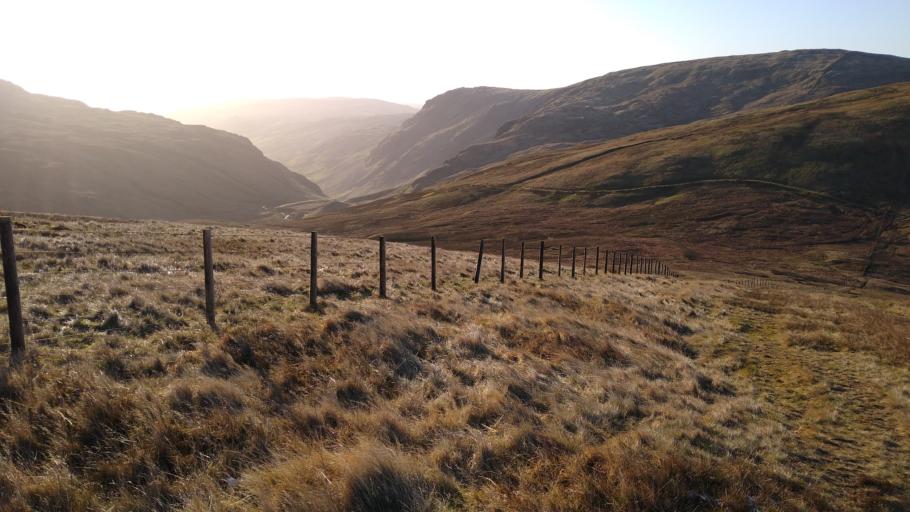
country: GB
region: England
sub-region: Cumbria
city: Windermere
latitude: 54.4793
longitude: -2.8094
